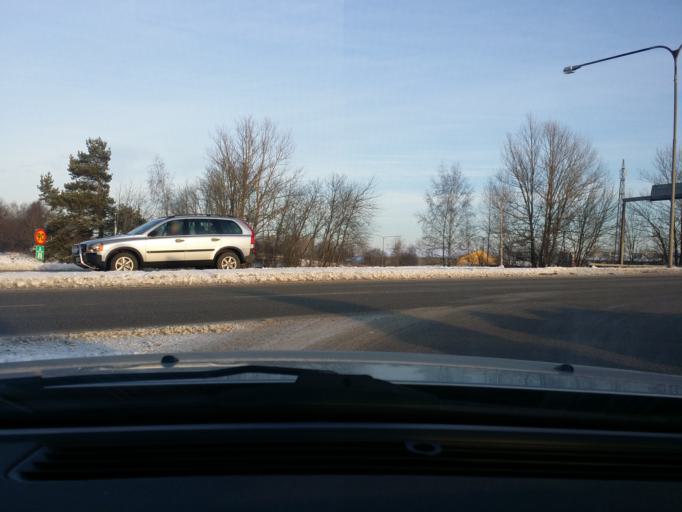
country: SE
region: OErebro
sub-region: Orebro Kommun
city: Orebro
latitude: 59.2764
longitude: 15.1774
